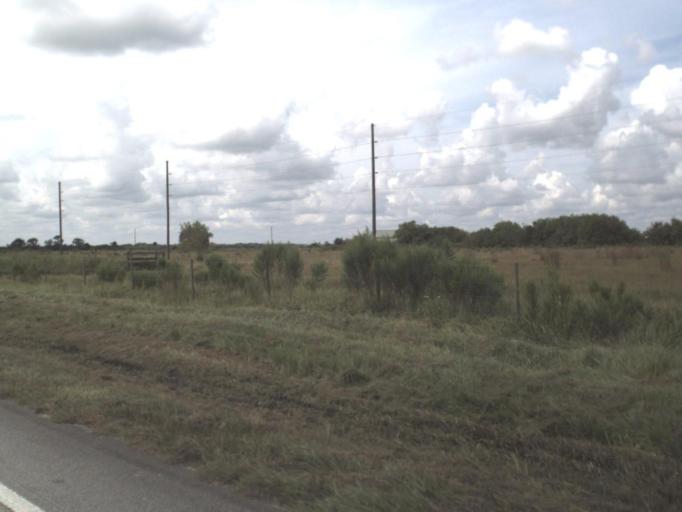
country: US
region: Florida
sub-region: Okeechobee County
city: Taylor Creek
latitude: 27.2653
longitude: -80.7384
